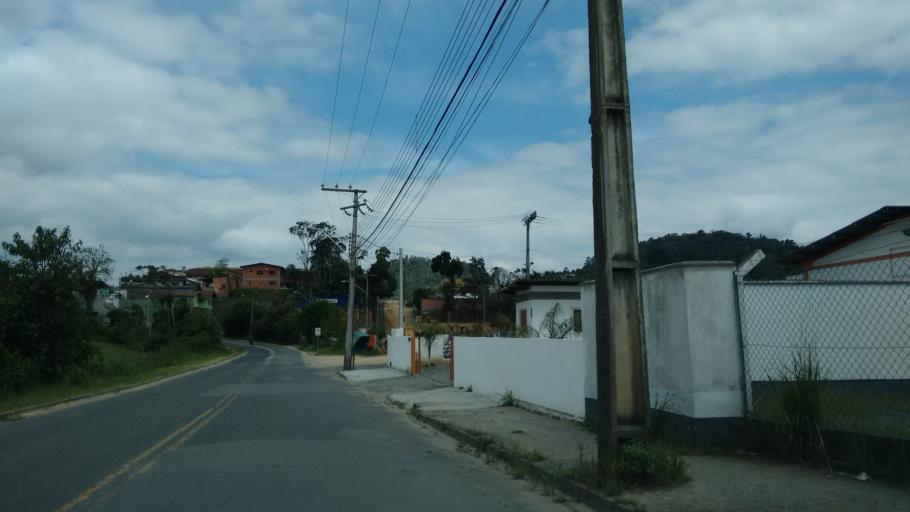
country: BR
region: Santa Catarina
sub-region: Blumenau
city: Blumenau
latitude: -26.8550
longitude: -49.1269
